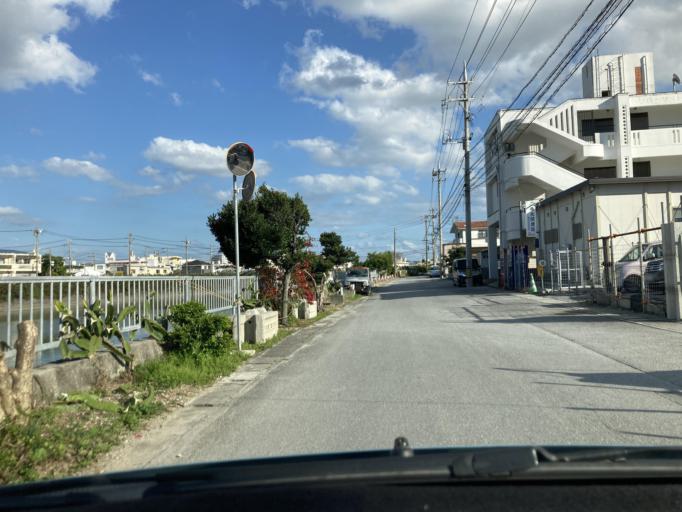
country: JP
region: Okinawa
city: Tomigusuku
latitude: 26.1950
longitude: 127.6995
